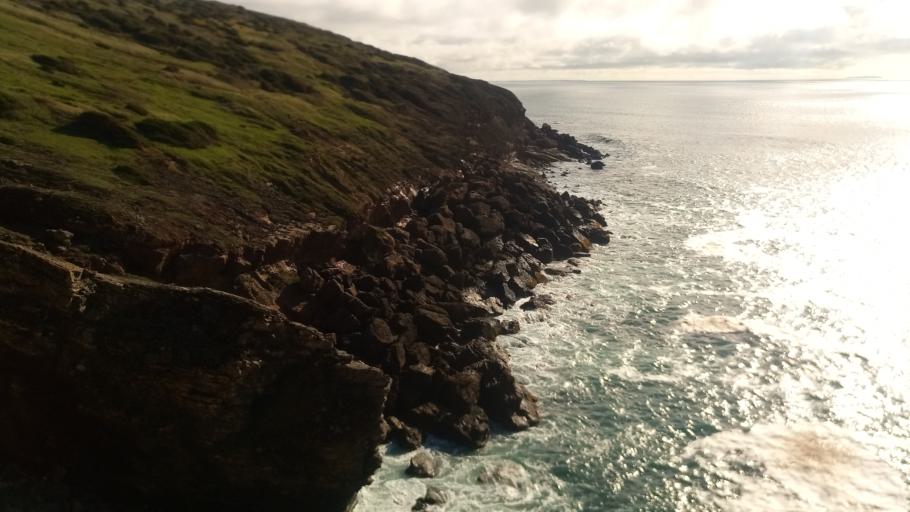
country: PT
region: Leiria
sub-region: Caldas da Rainha
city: Caldas da Rainha
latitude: 39.4950
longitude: -9.1755
